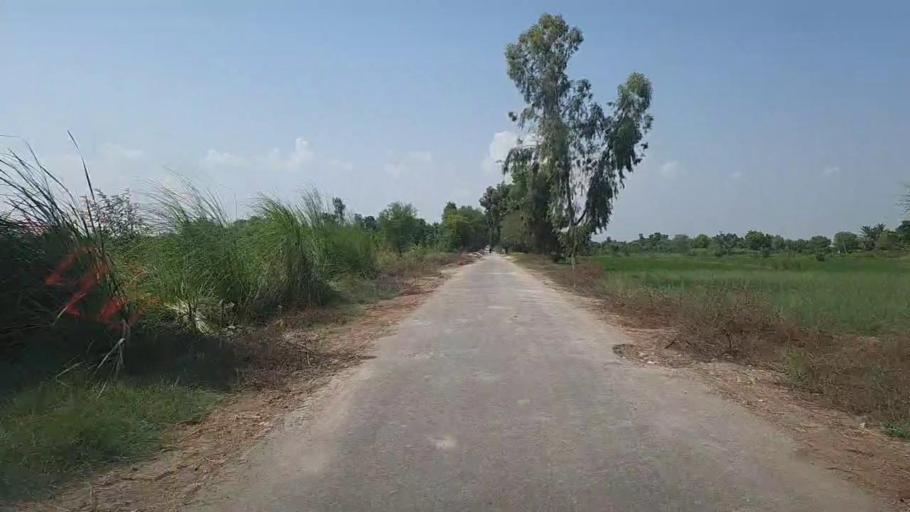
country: PK
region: Sindh
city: Khairpur
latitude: 28.0845
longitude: 69.6343
